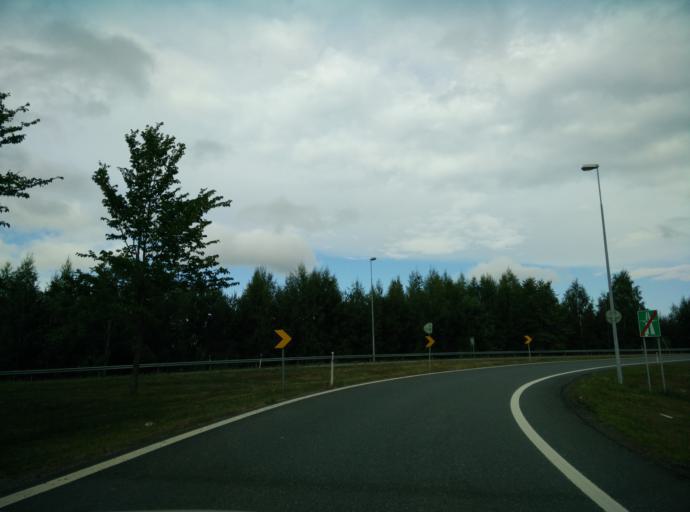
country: FI
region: Haeme
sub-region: Haemeenlinna
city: Kalvola
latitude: 61.0992
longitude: 24.1659
